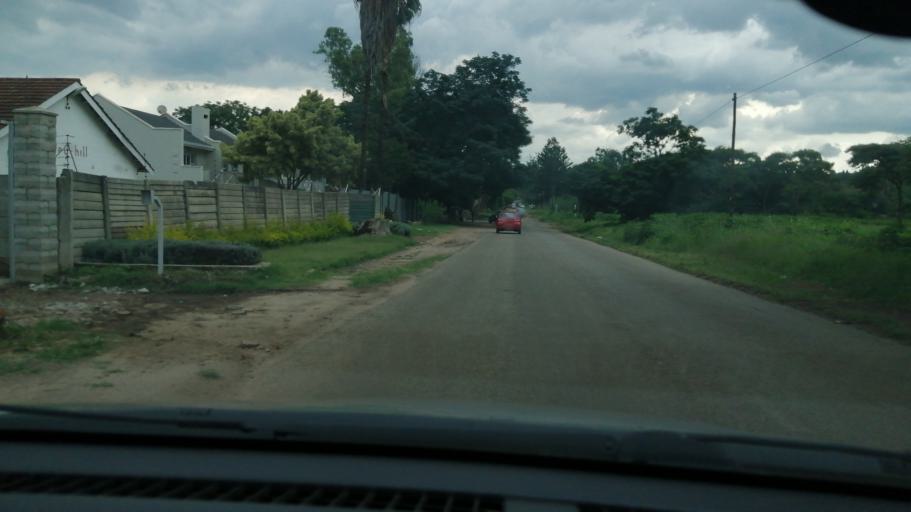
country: ZW
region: Harare
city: Harare
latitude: -17.7990
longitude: 31.0396
